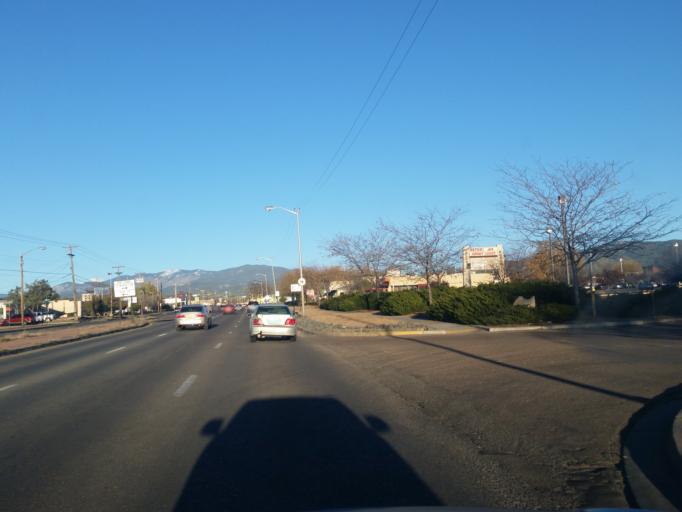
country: US
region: New Mexico
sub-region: Santa Fe County
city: Agua Fria
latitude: 35.6609
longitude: -105.9803
